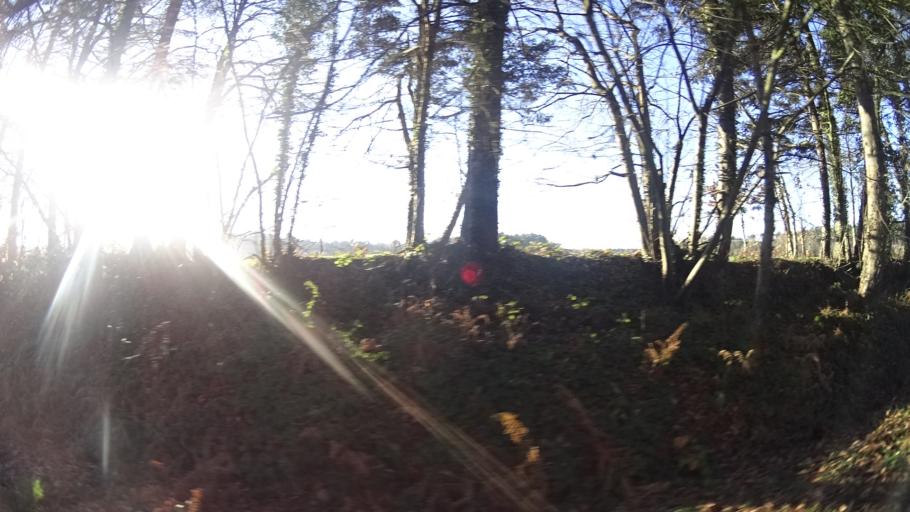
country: FR
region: Brittany
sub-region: Departement du Morbihan
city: Saint-Jacut-les-Pins
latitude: 47.6734
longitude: -2.1818
